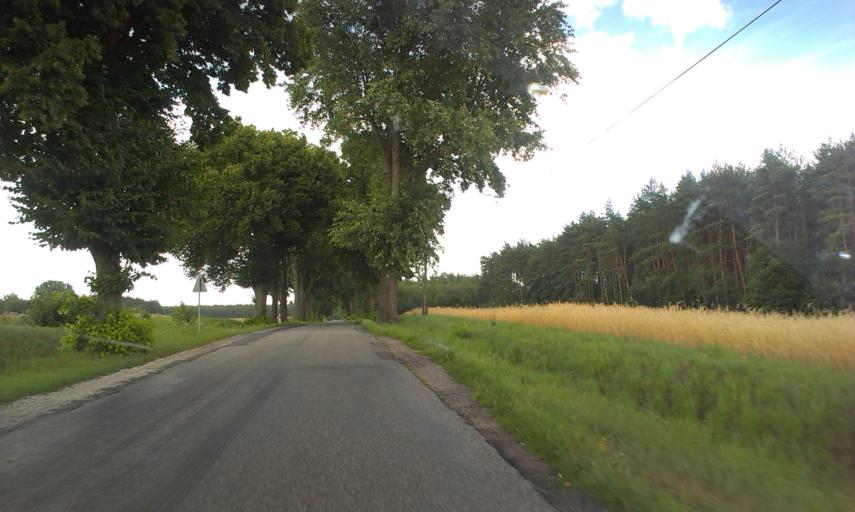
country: PL
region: Greater Poland Voivodeship
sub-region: Powiat zlotowski
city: Krajenka
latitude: 53.2869
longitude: 17.0061
